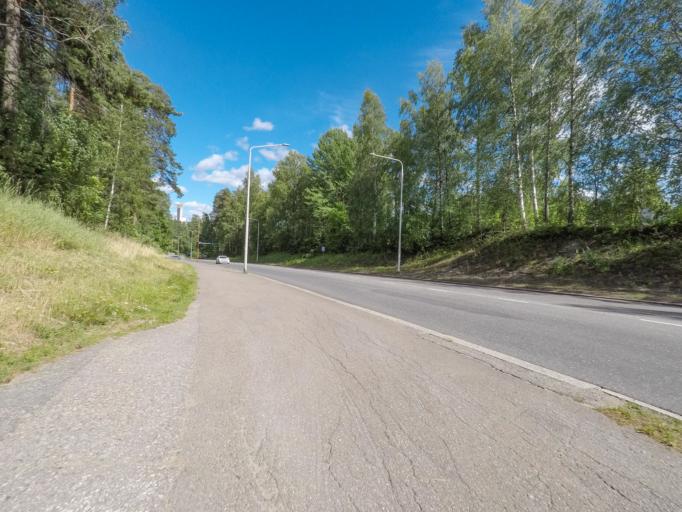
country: FI
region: South Karelia
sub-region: Lappeenranta
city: Lappeenranta
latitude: 61.0619
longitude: 28.2162
